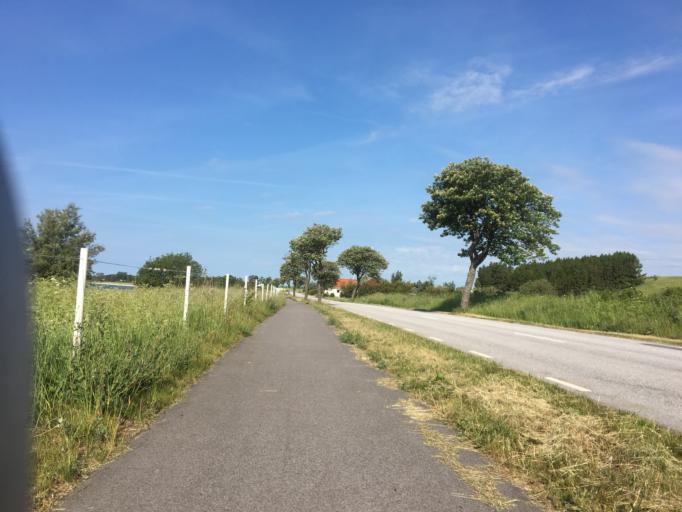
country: SE
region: Skane
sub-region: Skurups Kommun
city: Rydsgard
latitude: 55.4180
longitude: 13.6539
